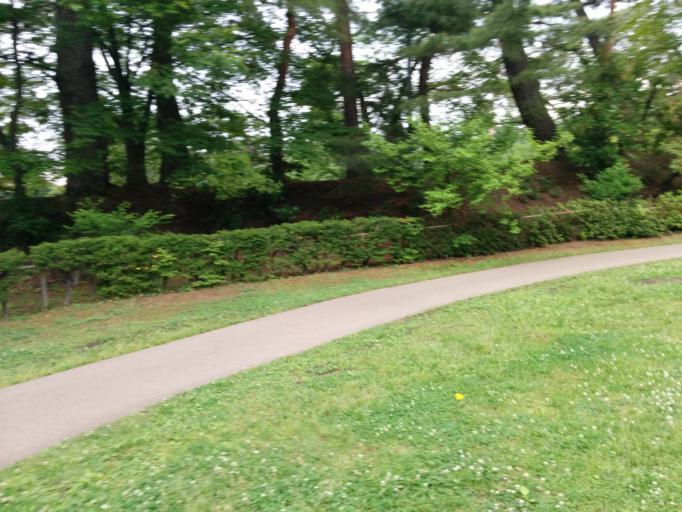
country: JP
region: Aomori
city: Hirosaki
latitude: 40.6098
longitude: 140.4649
